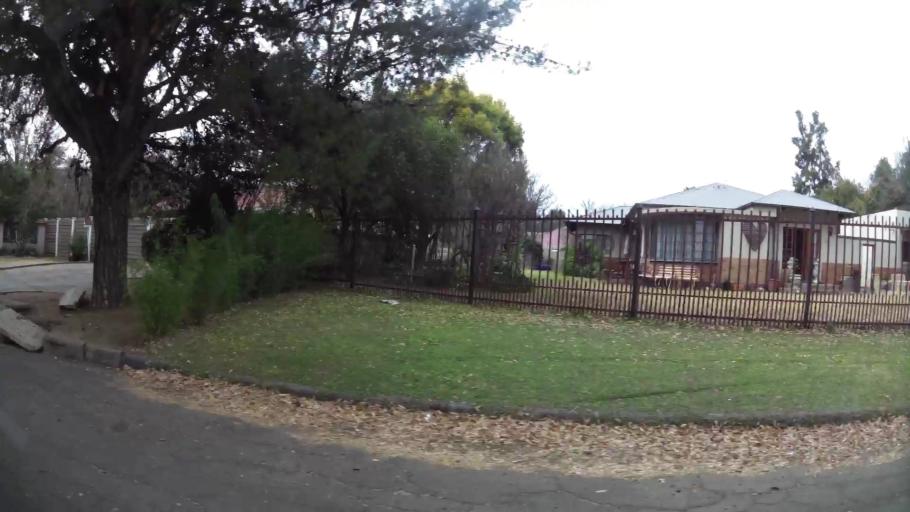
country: ZA
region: Orange Free State
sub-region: Mangaung Metropolitan Municipality
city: Bloemfontein
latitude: -29.1193
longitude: 26.1974
